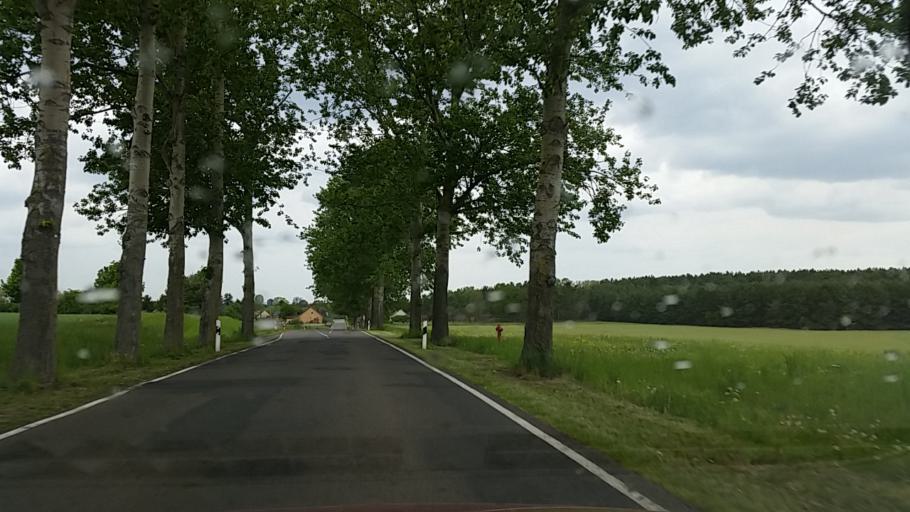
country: DE
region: Brandenburg
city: Rauen
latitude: 52.3198
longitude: 13.9611
